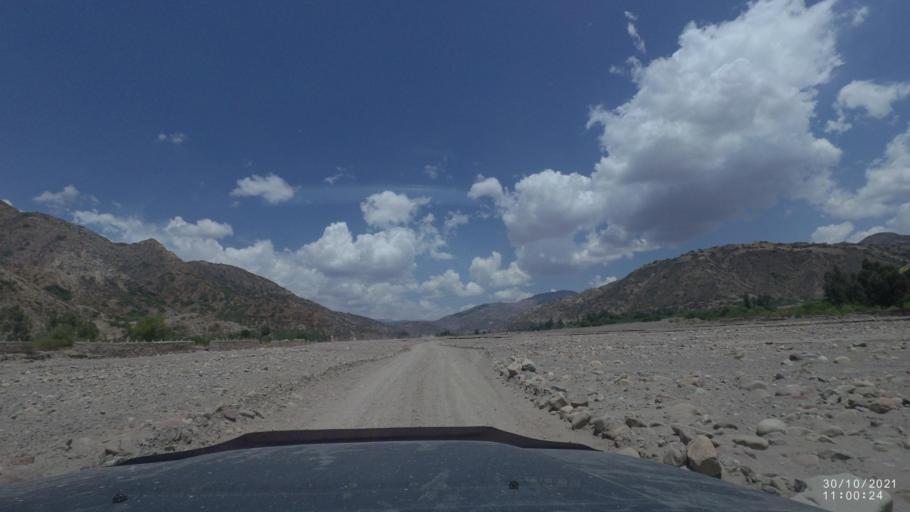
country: BO
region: Cochabamba
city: Sipe Sipe
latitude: -17.5359
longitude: -66.5153
